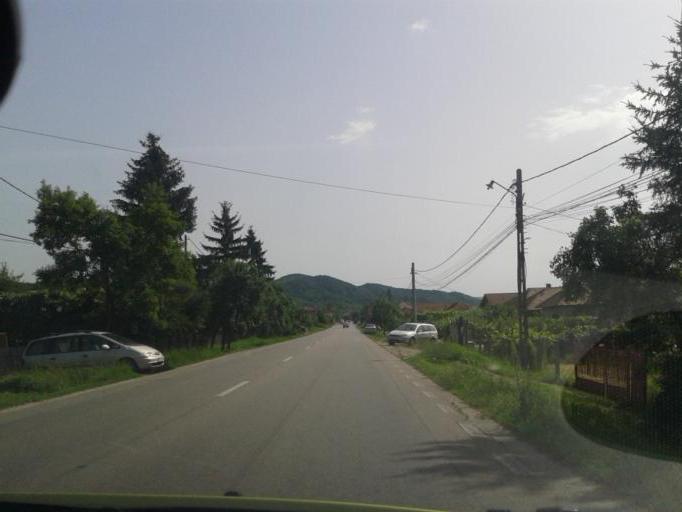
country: RO
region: Valcea
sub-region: Municipiul Ramnicu Valcea
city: Copacelu
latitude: 45.0643
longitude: 24.3046
